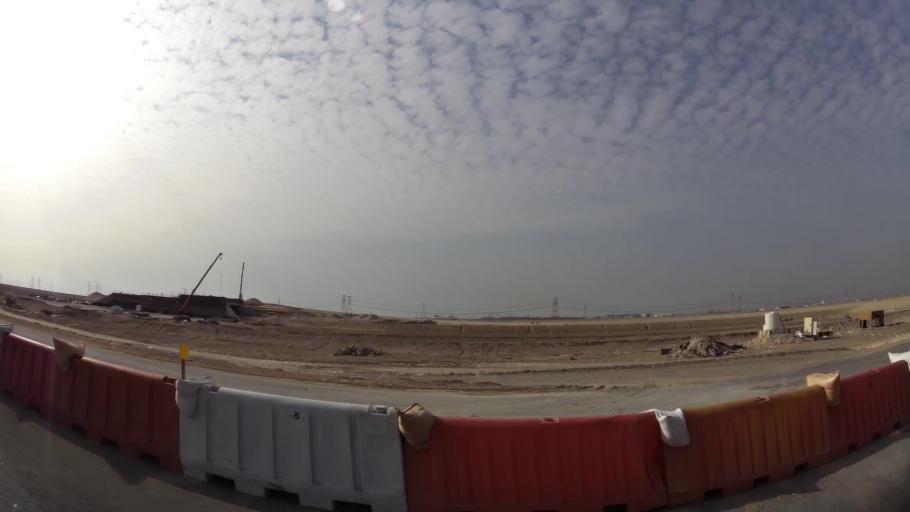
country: AE
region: Abu Dhabi
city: Abu Dhabi
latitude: 24.2477
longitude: 54.4740
